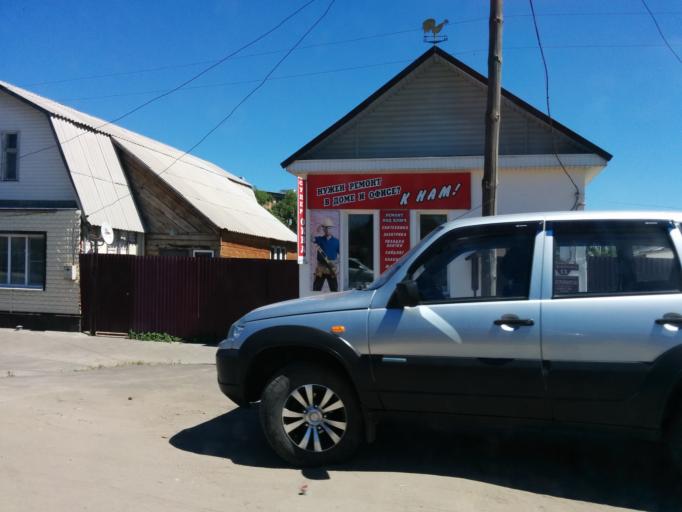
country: RU
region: Tambov
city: Morshansk
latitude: 53.4373
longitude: 41.8015
